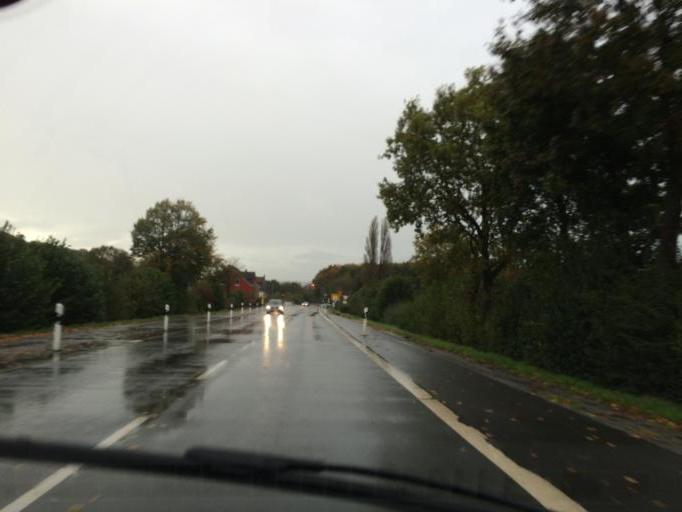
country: DE
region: North Rhine-Westphalia
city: Dorsten
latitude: 51.6801
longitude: 7.0178
